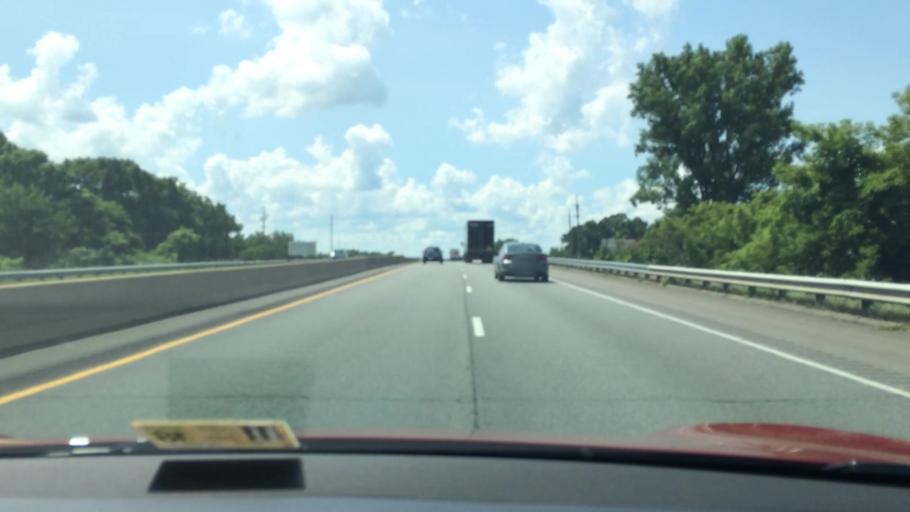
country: US
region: Indiana
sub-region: Saint Joseph County
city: South Bend
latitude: 41.6895
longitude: -86.3410
